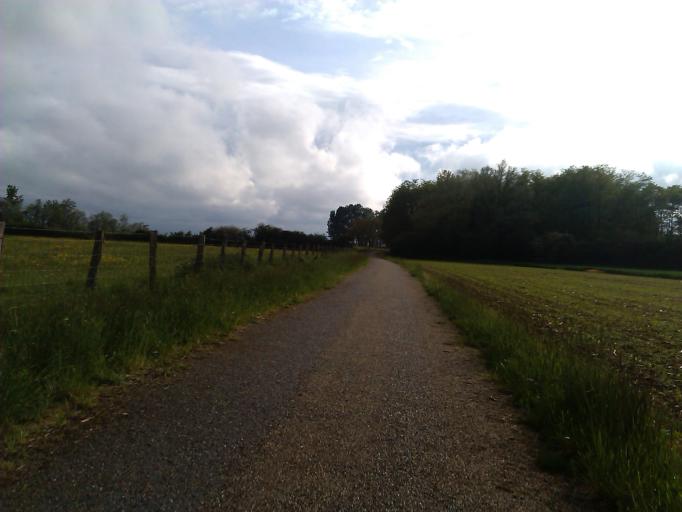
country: FR
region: Bourgogne
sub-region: Departement de Saone-et-Loire
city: Crissey
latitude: 46.8165
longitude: 4.9032
